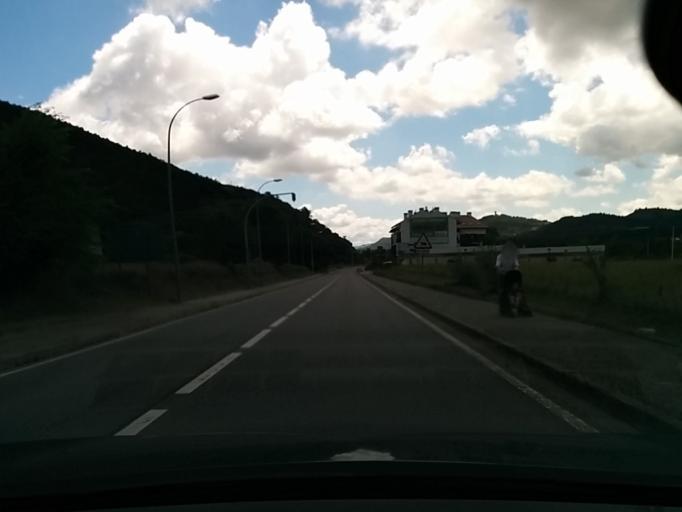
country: ES
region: Aragon
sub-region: Provincia de Huesca
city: Boltana
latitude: 42.4392
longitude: 0.0752
